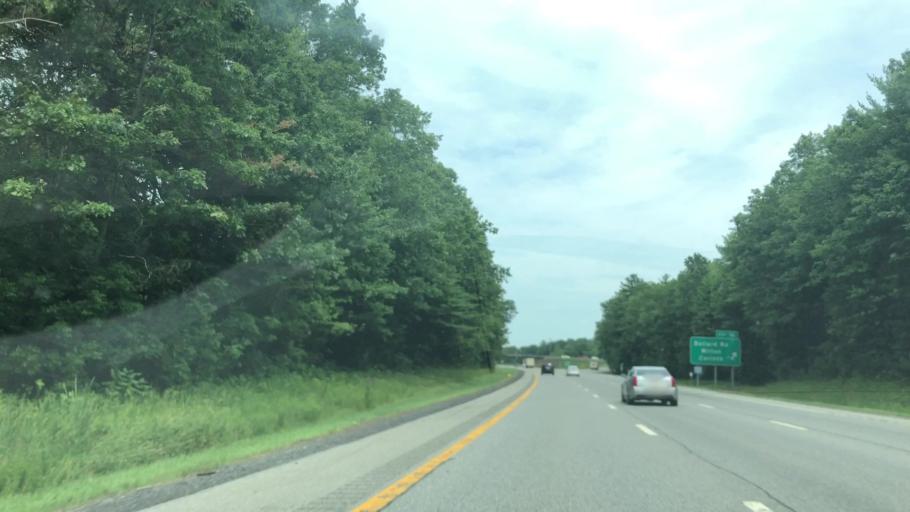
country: US
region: New York
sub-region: Saratoga County
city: Saratoga Springs
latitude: 43.1650
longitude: -73.7154
